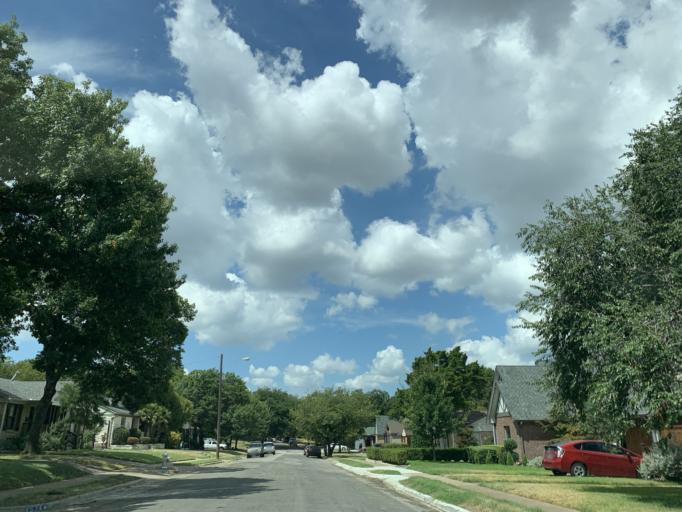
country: US
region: Texas
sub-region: Dallas County
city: Cockrell Hill
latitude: 32.7470
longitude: -96.8601
